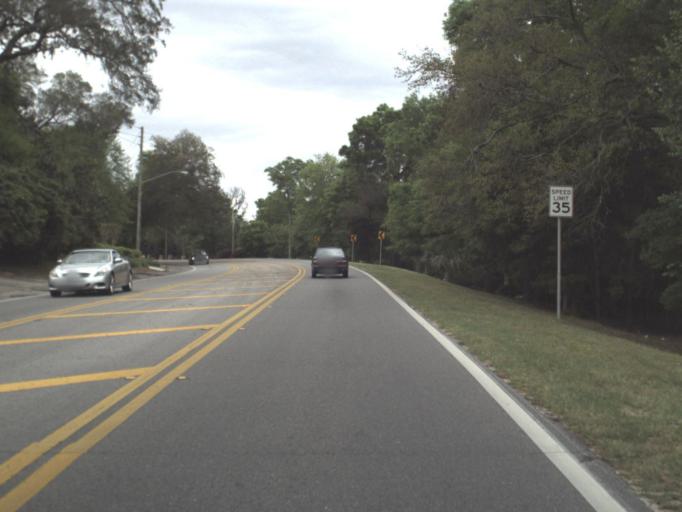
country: US
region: Florida
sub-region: Escambia County
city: East Pensacola Heights
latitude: 30.4518
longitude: -87.1932
